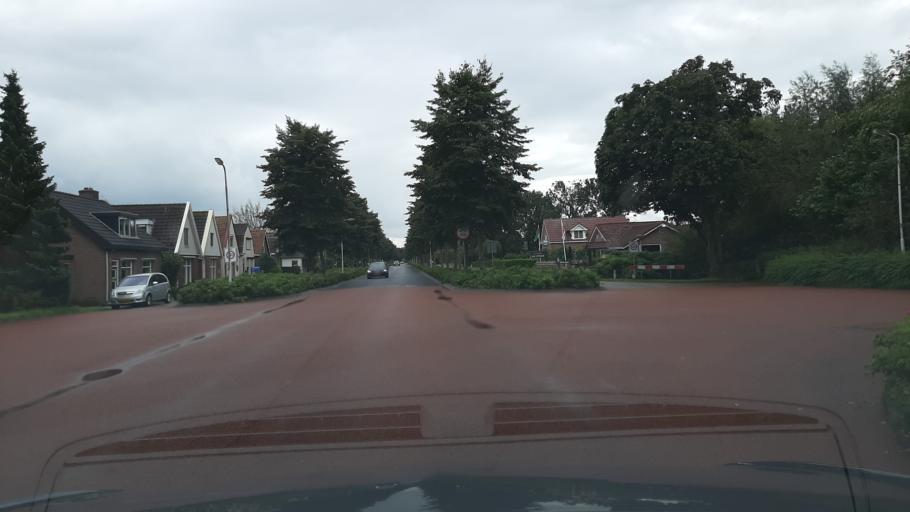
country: NL
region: Friesland
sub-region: Gemeente Weststellingwerf
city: Wolvega
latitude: 52.8910
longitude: 5.9997
